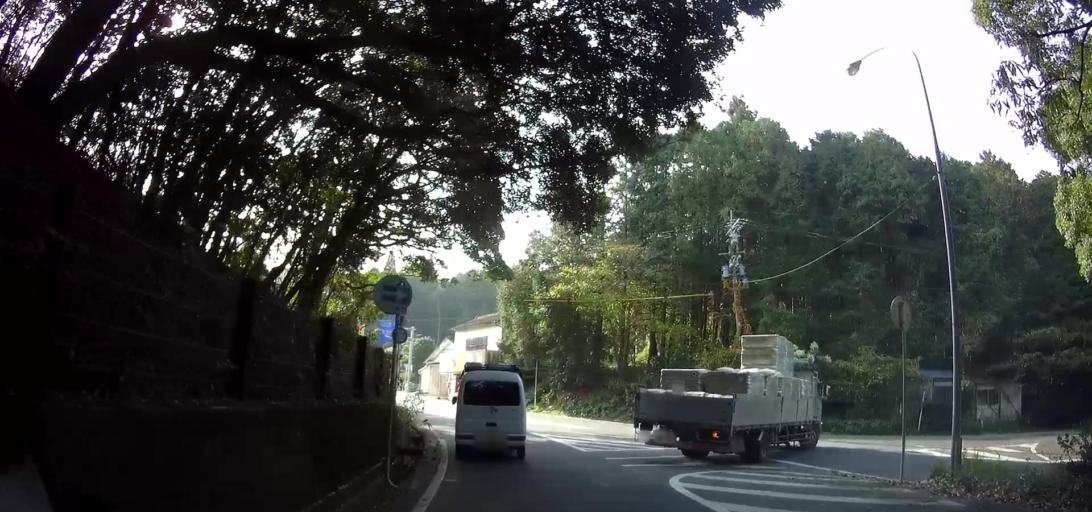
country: JP
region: Nagasaki
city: Shimabara
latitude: 32.6772
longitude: 130.1944
